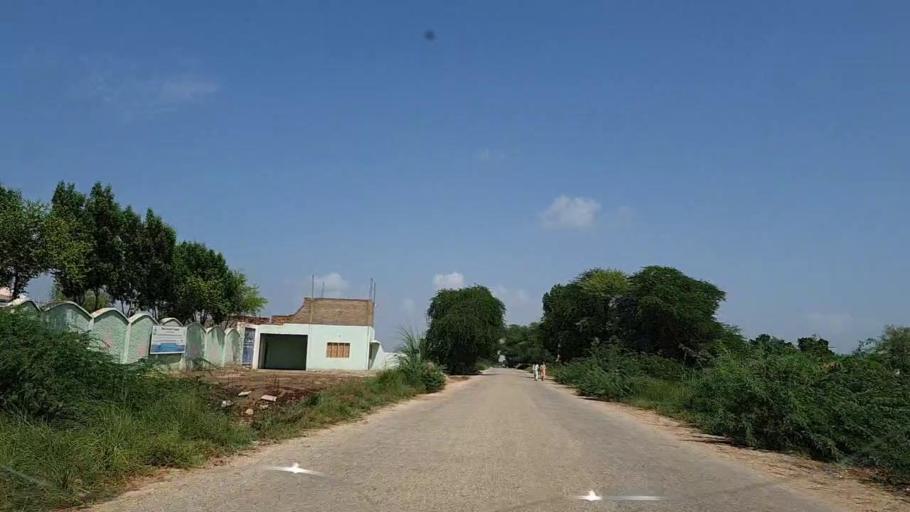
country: PK
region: Sindh
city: Pad Idan
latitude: 26.7934
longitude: 68.2465
